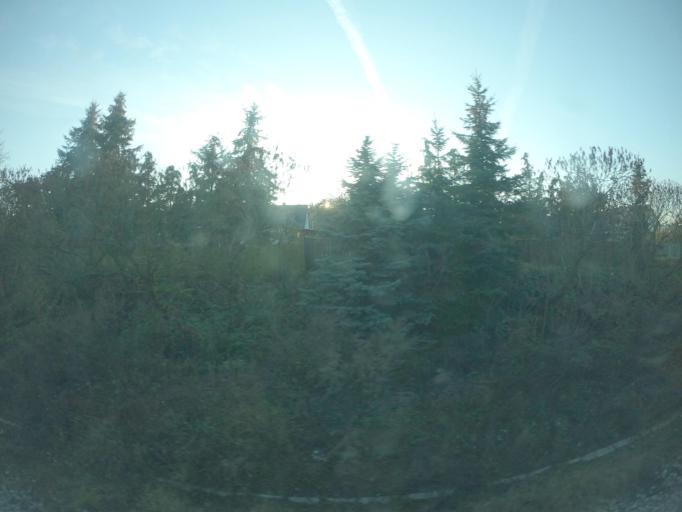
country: PL
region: Lubusz
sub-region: Powiat slubicki
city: Rzepin
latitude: 52.3480
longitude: 14.8233
